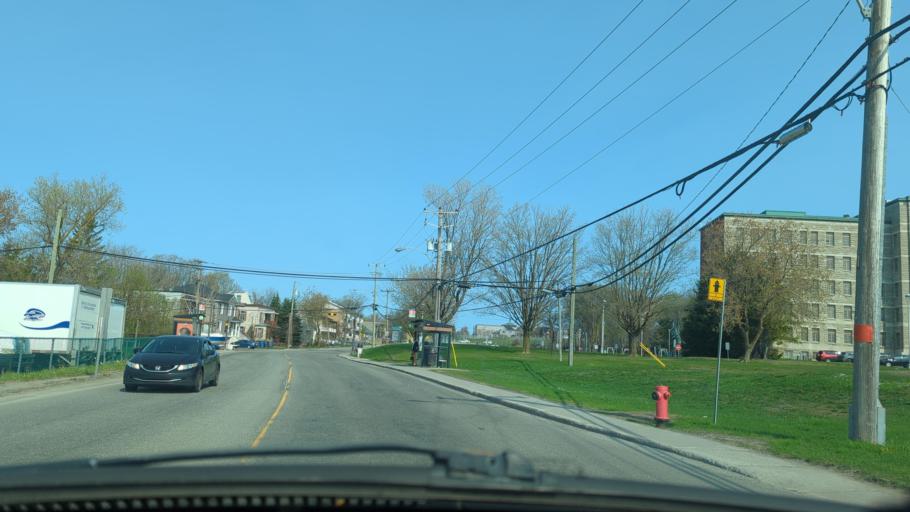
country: CA
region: Quebec
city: Quebec
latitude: 46.8508
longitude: -71.2227
